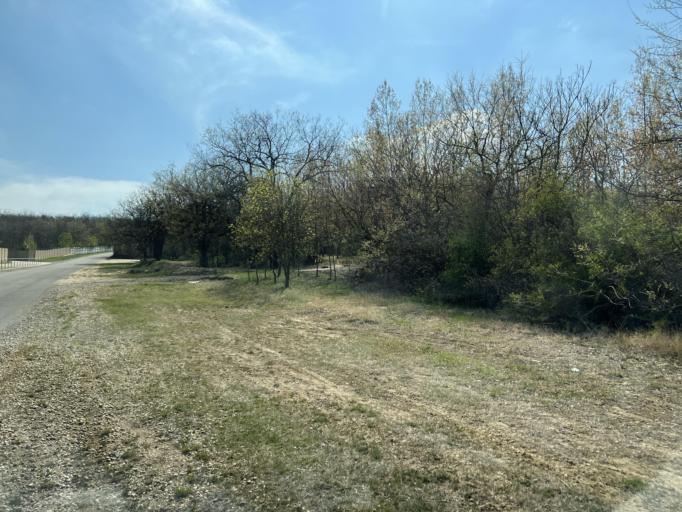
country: HU
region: Pest
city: Mogyorod
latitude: 47.5827
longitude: 19.2414
